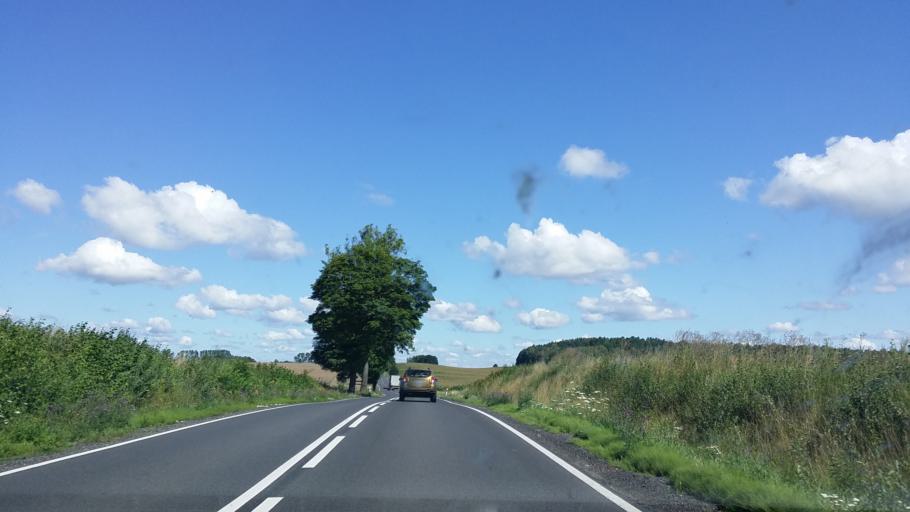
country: PL
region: West Pomeranian Voivodeship
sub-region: Powiat drawski
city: Kalisz Pomorski
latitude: 53.3135
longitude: 15.9080
